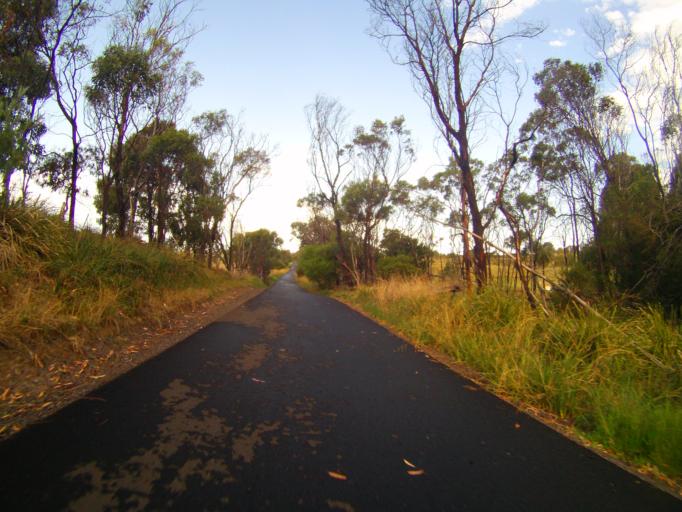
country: AU
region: Victoria
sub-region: Greater Geelong
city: Clifton Springs
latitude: -38.1795
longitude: 144.5345
